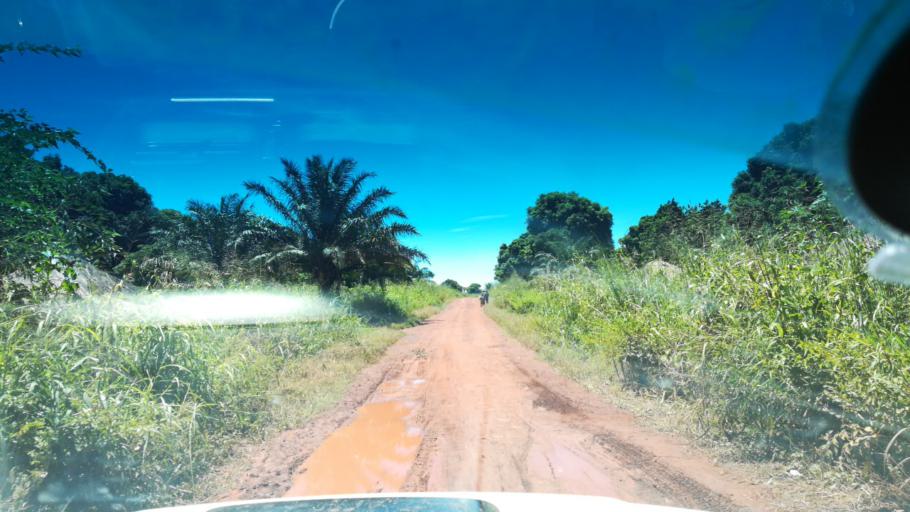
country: ZM
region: Luapula
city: Nchelenge
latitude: -8.8120
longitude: 28.6038
